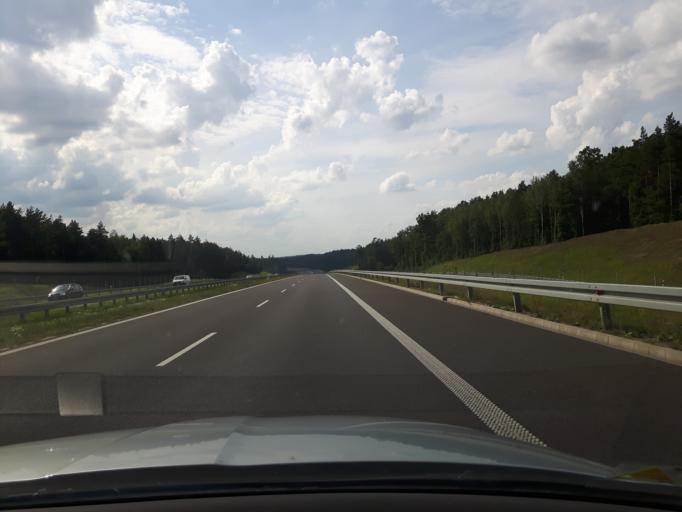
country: PL
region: Warmian-Masurian Voivodeship
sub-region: Powiat ostrodzki
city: Gierzwald
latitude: 53.5871
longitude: 20.1533
